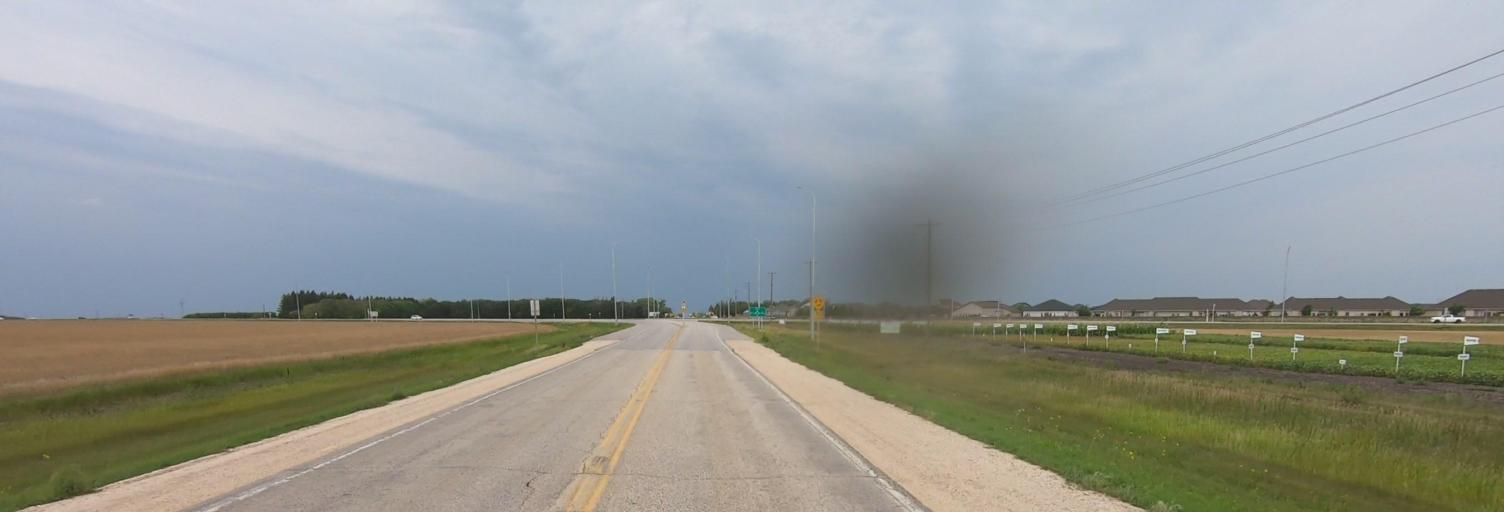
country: CA
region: Manitoba
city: Headingley
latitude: 49.7685
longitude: -97.3243
